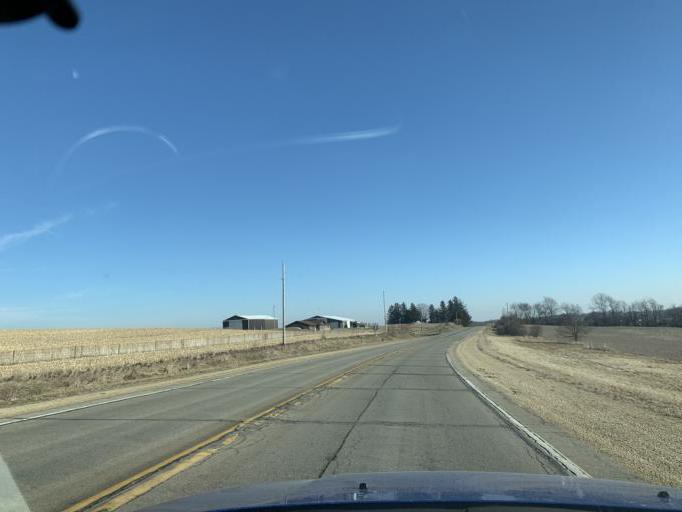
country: US
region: Wisconsin
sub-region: Green County
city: Monroe
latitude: 42.6105
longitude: -89.6142
